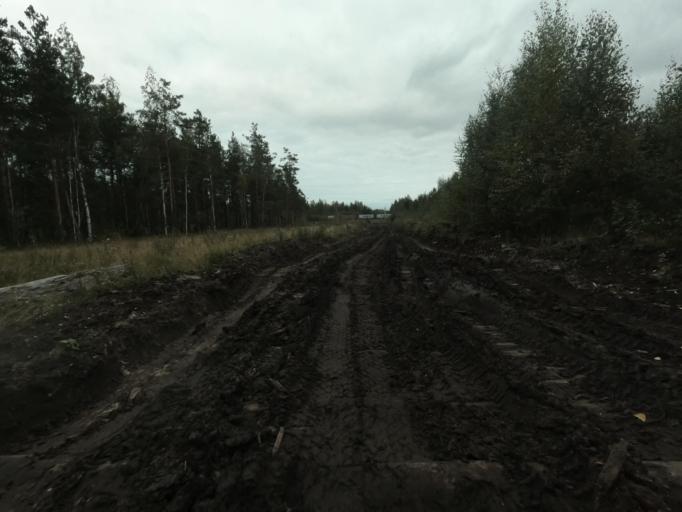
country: RU
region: St.-Petersburg
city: Sapernyy
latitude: 59.7636
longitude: 30.7232
